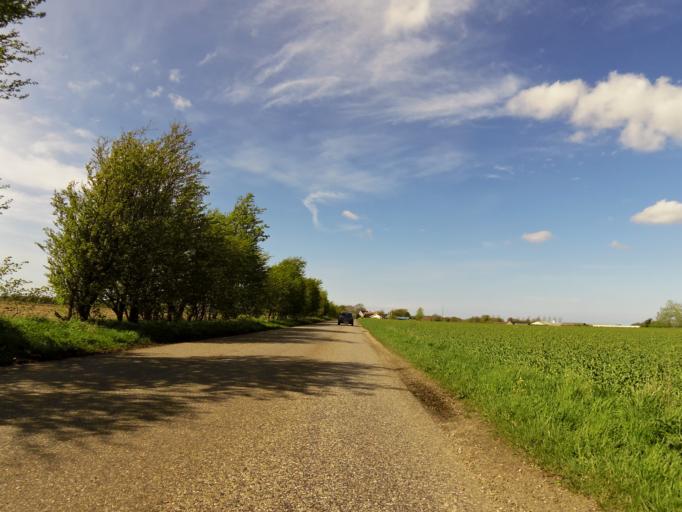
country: DK
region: Central Jutland
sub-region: Skive Kommune
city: Skive
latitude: 56.4647
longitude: 8.9730
